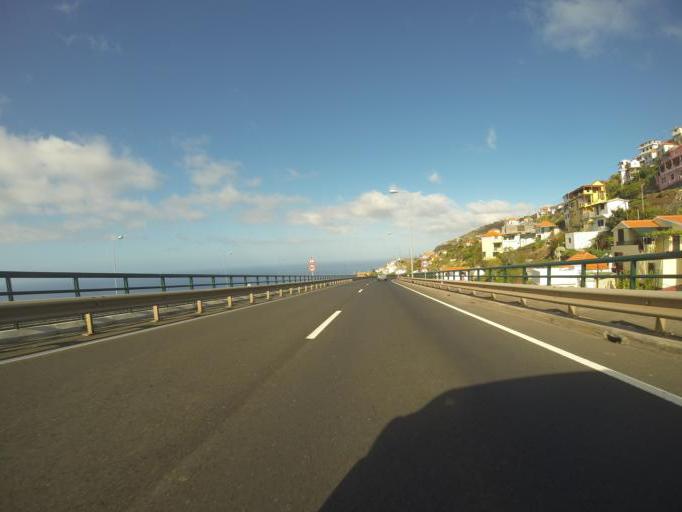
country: PT
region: Madeira
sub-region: Ribeira Brava
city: Campanario
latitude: 32.6656
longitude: -17.0375
